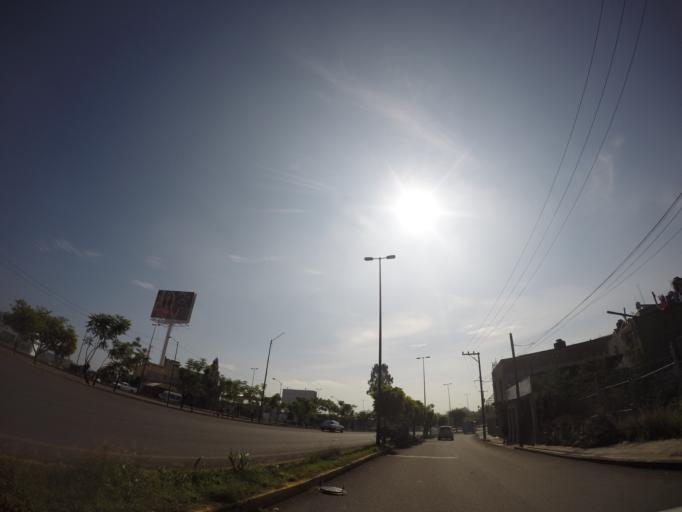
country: MX
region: Michoacan
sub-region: Tarimbaro
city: Fraccionamiento Metropolis II
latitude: 19.7272
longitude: -101.2216
